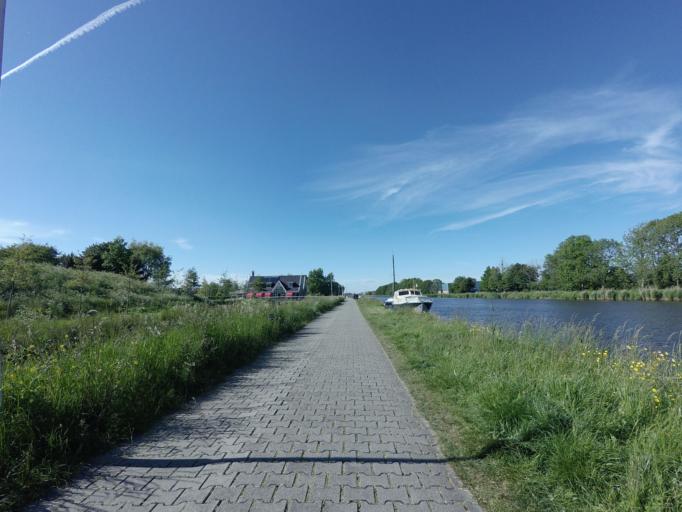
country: NL
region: North Holland
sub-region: Gemeente Zaanstad
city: Zaanstad
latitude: 52.5093
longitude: 4.7765
